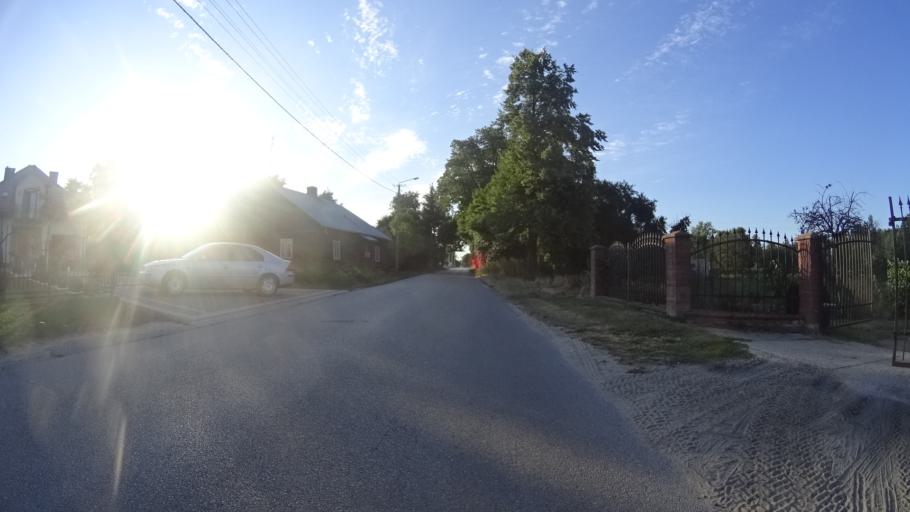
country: PL
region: Masovian Voivodeship
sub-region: Powiat grojecki
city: Goszczyn
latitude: 51.6940
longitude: 20.8157
